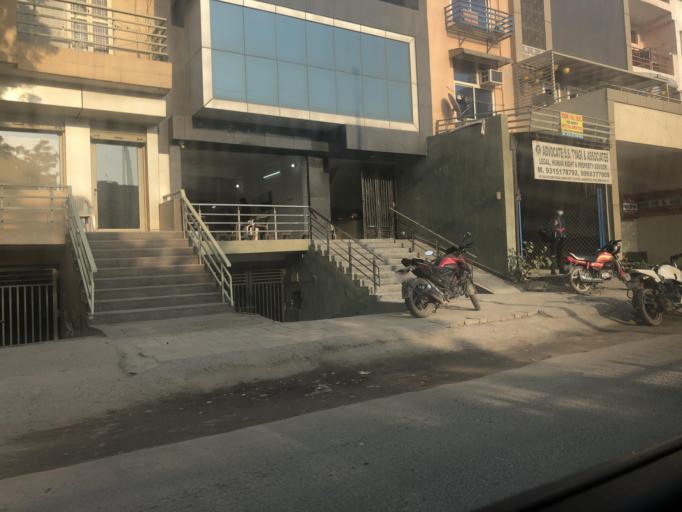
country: IN
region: Haryana
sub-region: Gurgaon
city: Gurgaon
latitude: 28.5309
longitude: 77.0861
